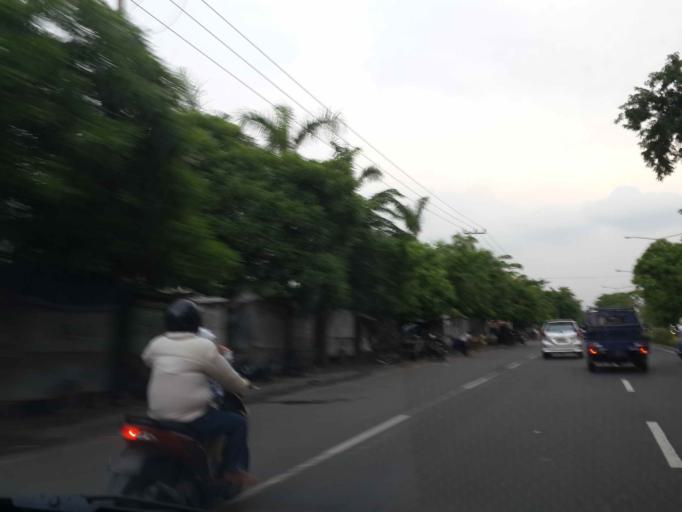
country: ID
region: East Java
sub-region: Kota Surabaya
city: Surabaya
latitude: -7.2465
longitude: 112.7209
